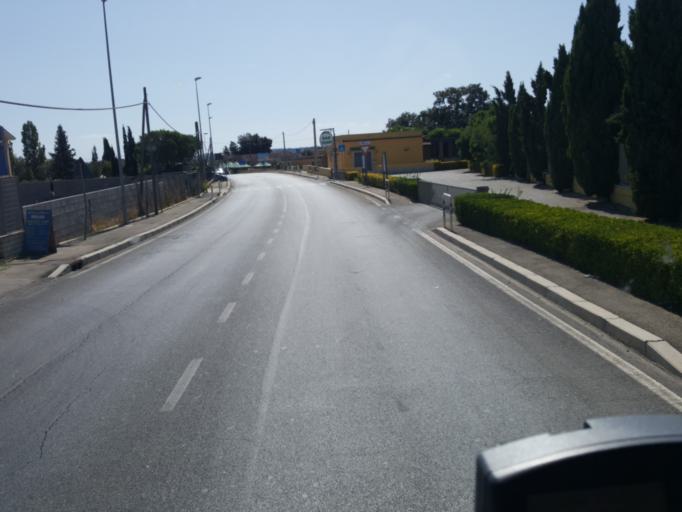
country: IT
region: Latium
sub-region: Citta metropolitana di Roma Capitale
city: Nettuno
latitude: 41.5033
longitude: 12.6868
